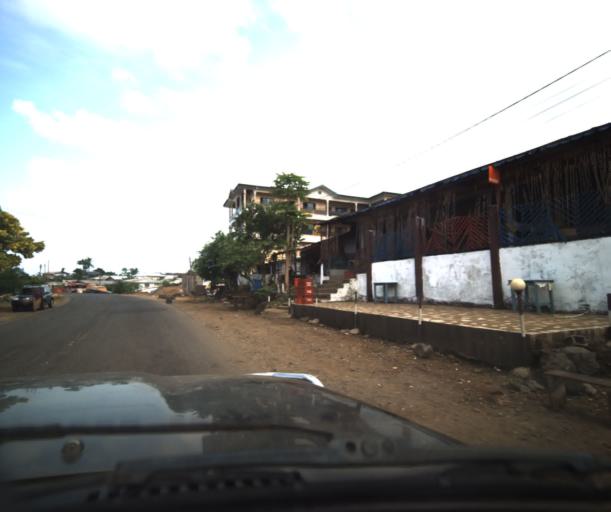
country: CM
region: South-West Province
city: Limbe
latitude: 4.0194
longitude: 9.1362
